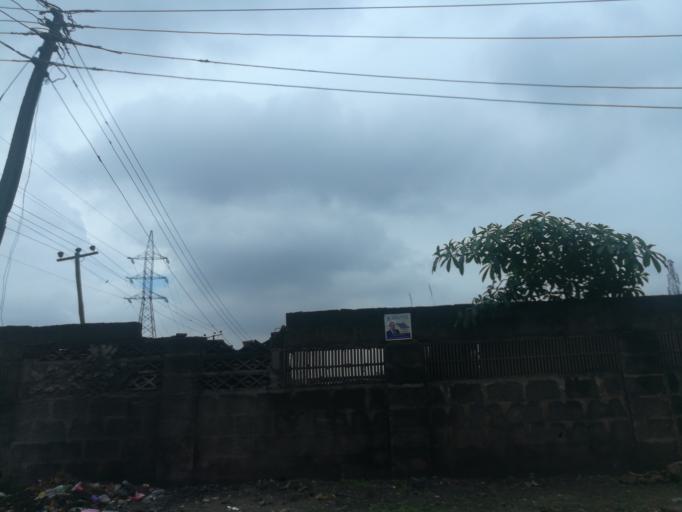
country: NG
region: Lagos
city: Ojota
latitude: 6.5757
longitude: 3.3745
